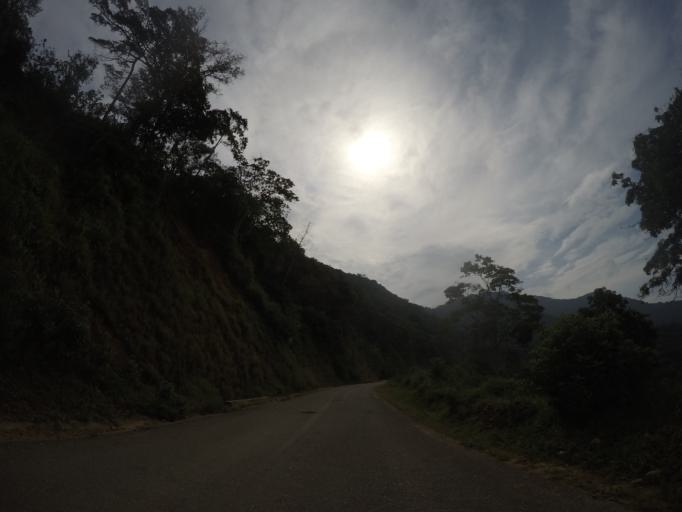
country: MX
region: Oaxaca
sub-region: San Pedro Pochutla
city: Los Naranjos Esquipulas
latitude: 15.9585
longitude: -96.4572
